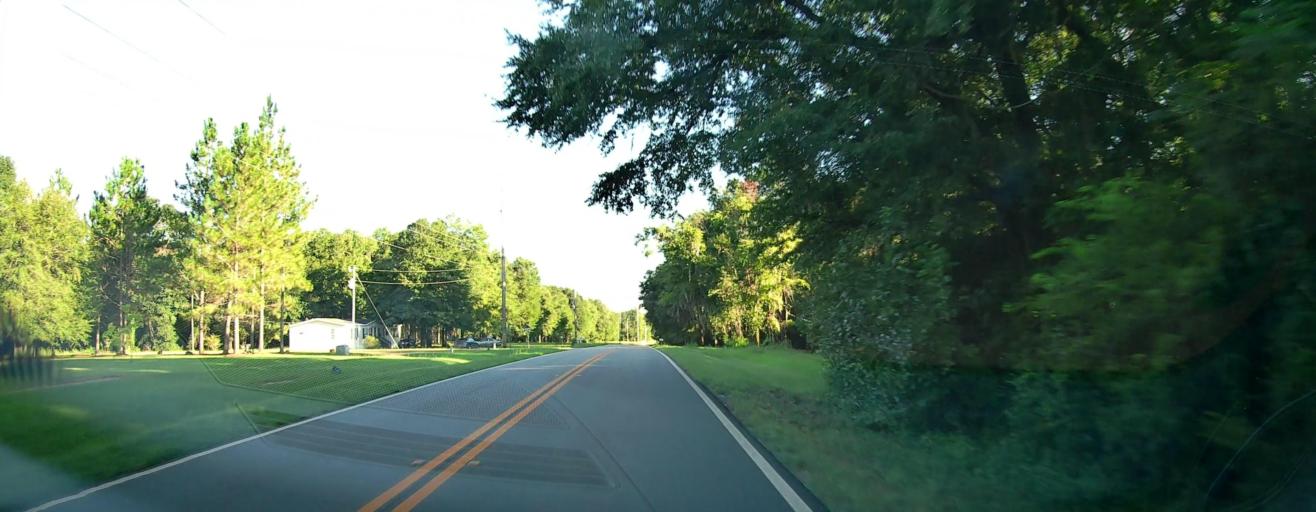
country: US
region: Georgia
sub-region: Pulaski County
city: Hawkinsville
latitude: 32.2945
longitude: -83.4497
